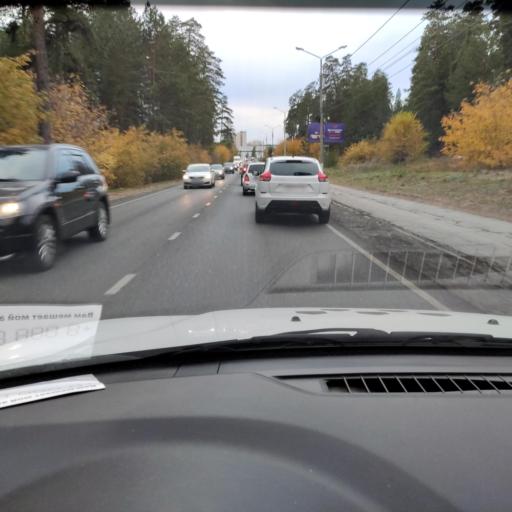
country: RU
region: Samara
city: Tol'yatti
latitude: 53.4761
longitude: 49.3312
